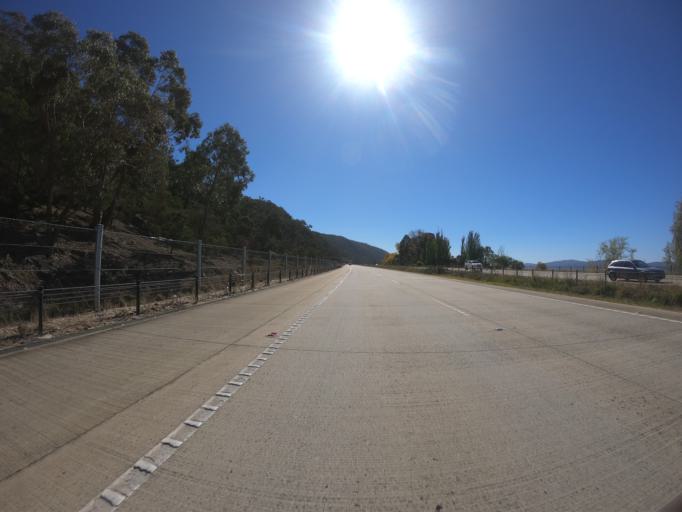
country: AU
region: New South Wales
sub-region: Yass Valley
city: Gundaroo
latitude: -35.0744
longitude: 149.3743
